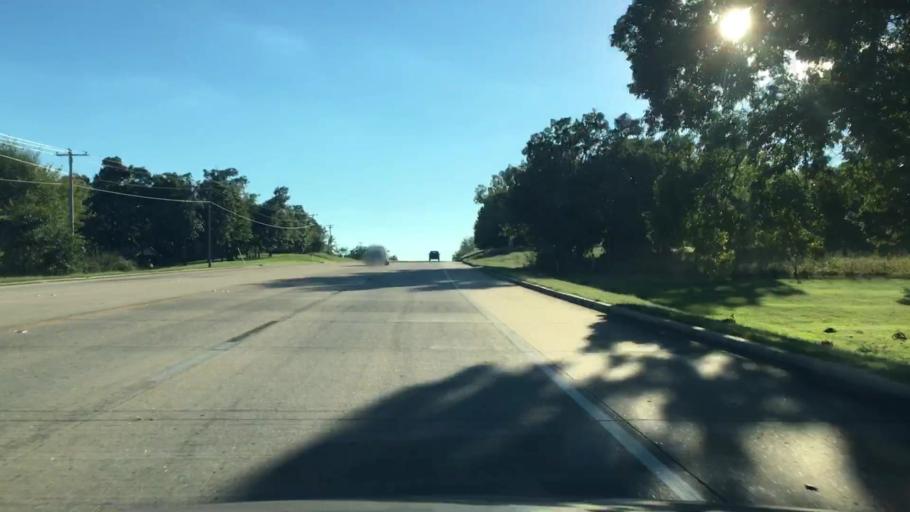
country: US
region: Oklahoma
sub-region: Cherokee County
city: Park Hill
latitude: 35.8186
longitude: -95.0563
